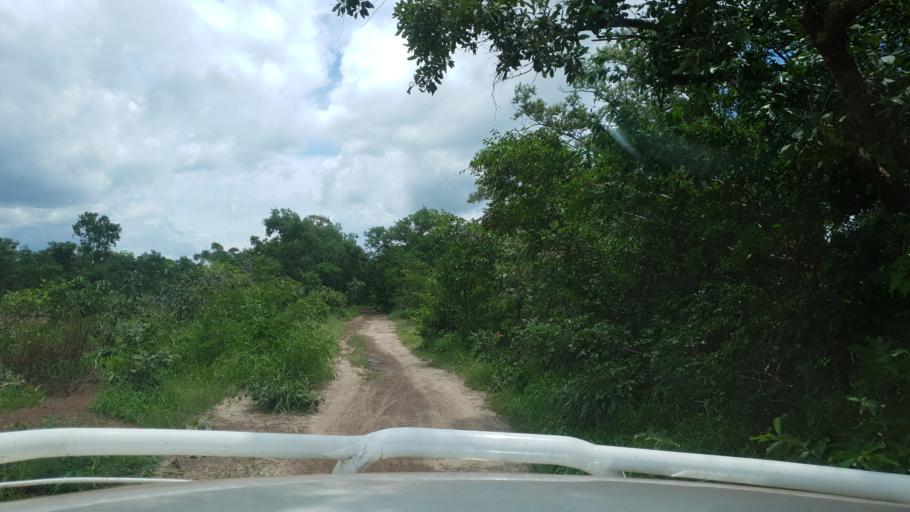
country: ML
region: Koulikoro
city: Banamba
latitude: 13.1968
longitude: -7.3245
